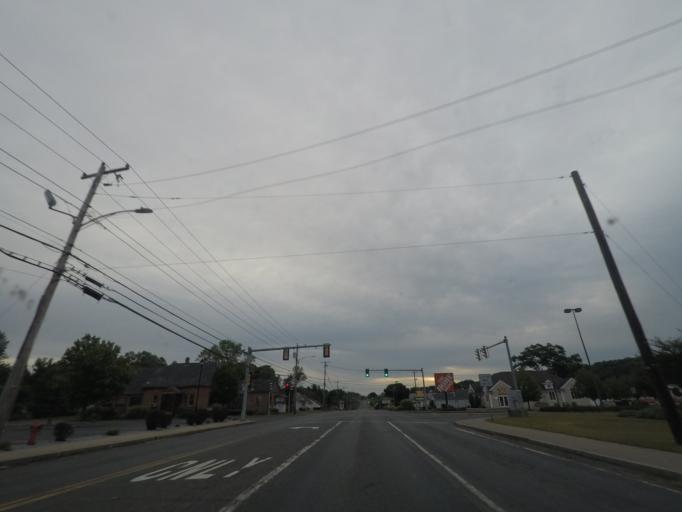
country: US
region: Massachusetts
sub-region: Hampden County
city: Ludlow
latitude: 42.1493
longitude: -72.4753
